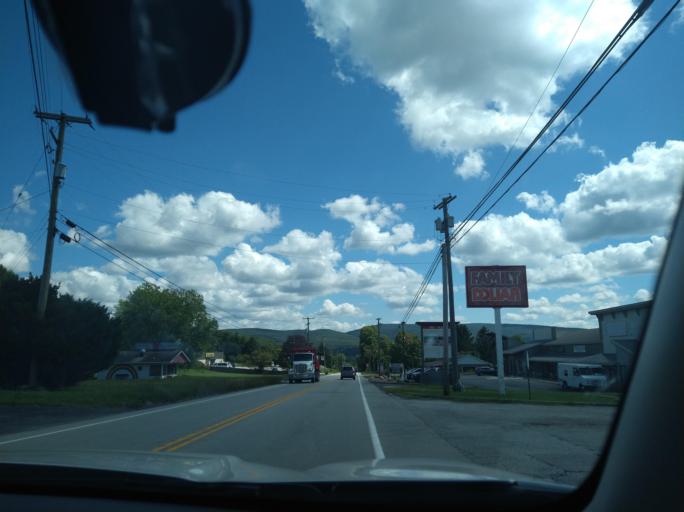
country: US
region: Pennsylvania
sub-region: Fayette County
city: Bear Rocks
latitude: 40.0987
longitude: -79.3600
